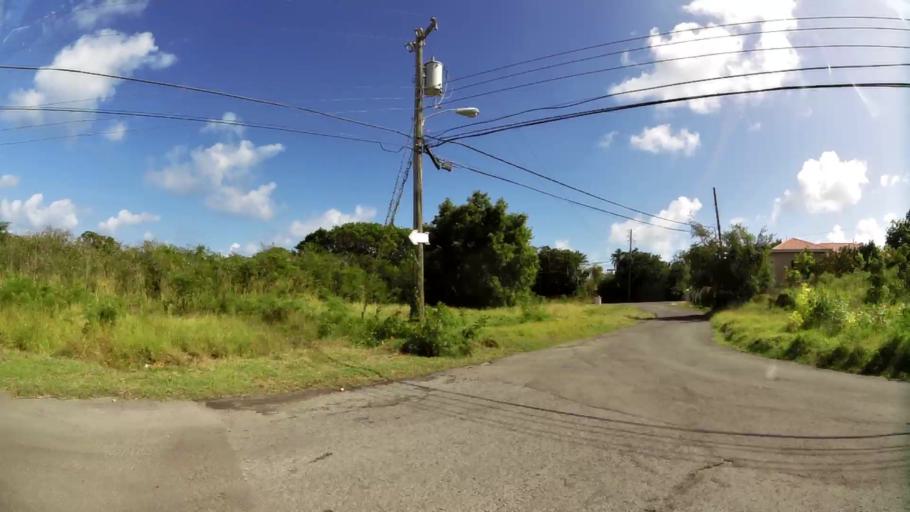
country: AG
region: Saint George
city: Piggotts
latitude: 17.1666
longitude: -61.8029
